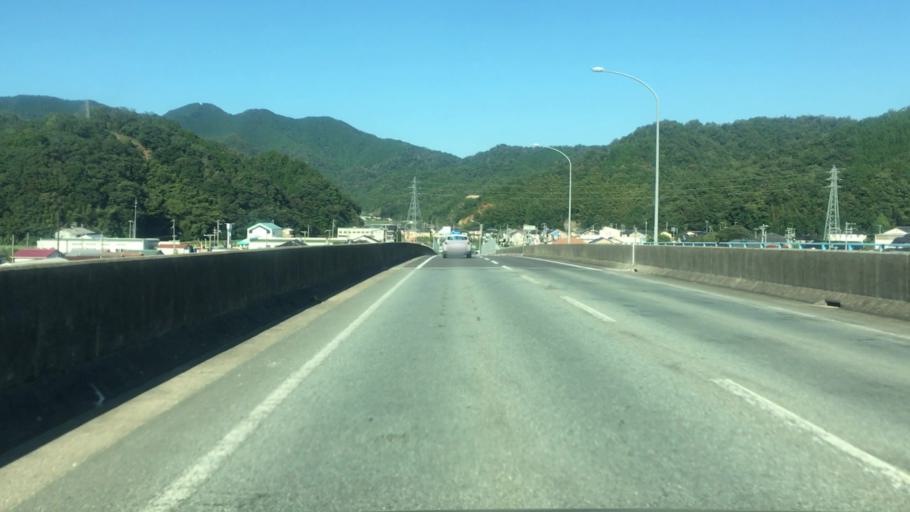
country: JP
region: Hyogo
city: Toyooka
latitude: 35.5569
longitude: 134.8215
